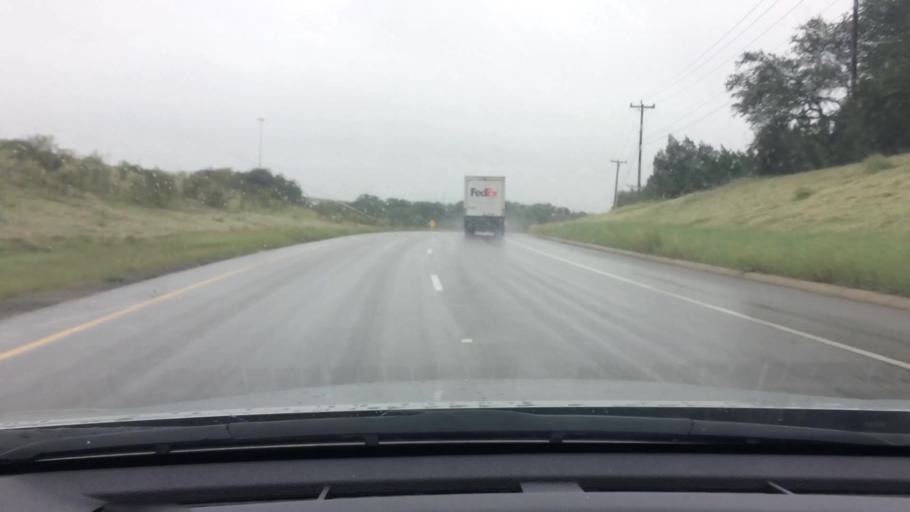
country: US
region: Texas
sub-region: Bexar County
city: Leon Valley
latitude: 29.4824
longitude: -98.7069
